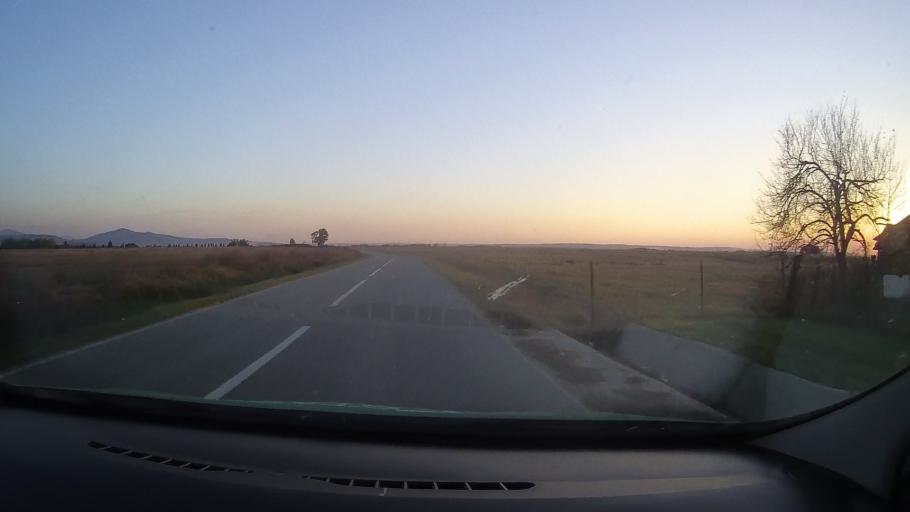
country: RO
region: Timis
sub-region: Comuna Manastiur
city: Manastiur
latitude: 45.8234
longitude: 22.0712
